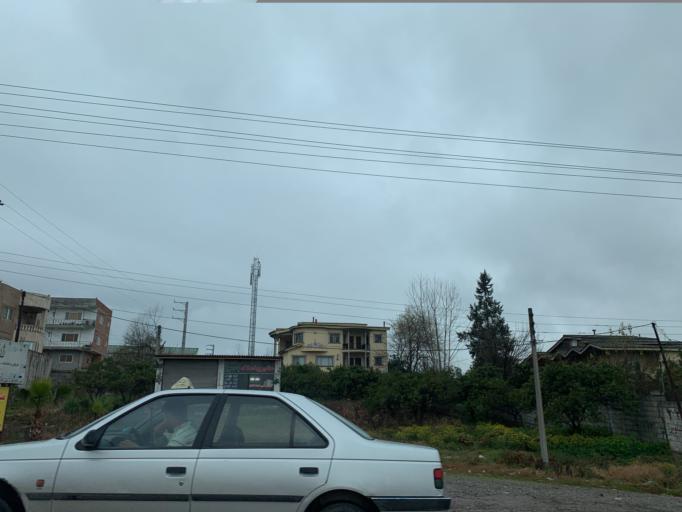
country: IR
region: Mazandaran
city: Amol
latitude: 36.4048
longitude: 52.3471
